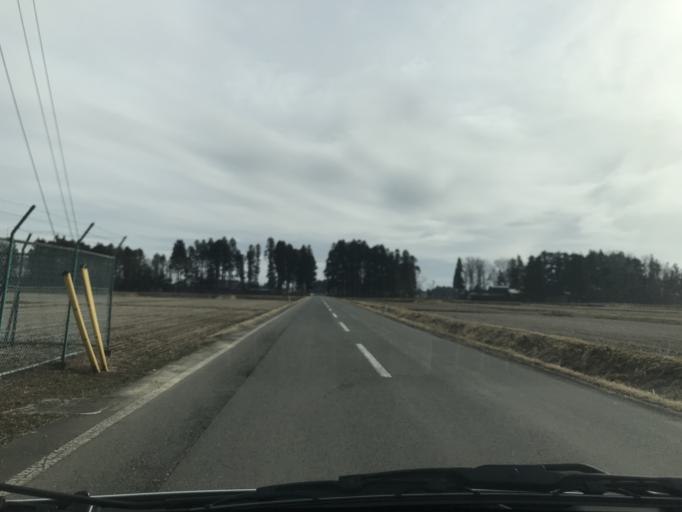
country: JP
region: Iwate
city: Hanamaki
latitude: 39.4176
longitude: 141.0808
